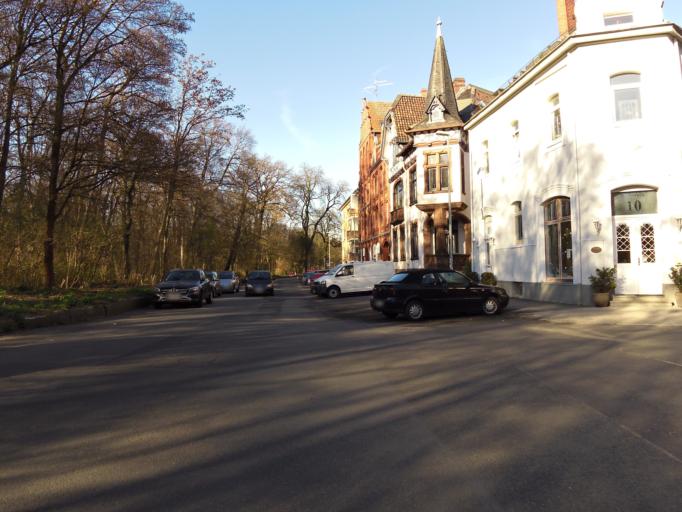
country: DE
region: Lower Saxony
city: Hannover
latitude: 52.3740
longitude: 9.7830
